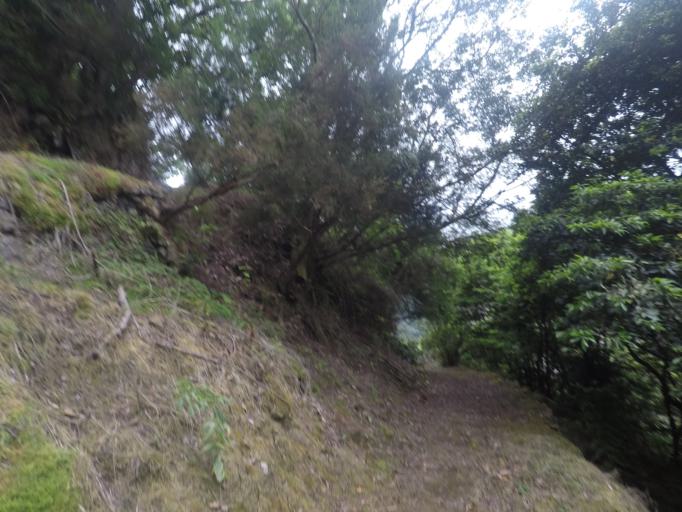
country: PT
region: Madeira
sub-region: Santana
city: Santana
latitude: 32.7546
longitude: -16.8742
